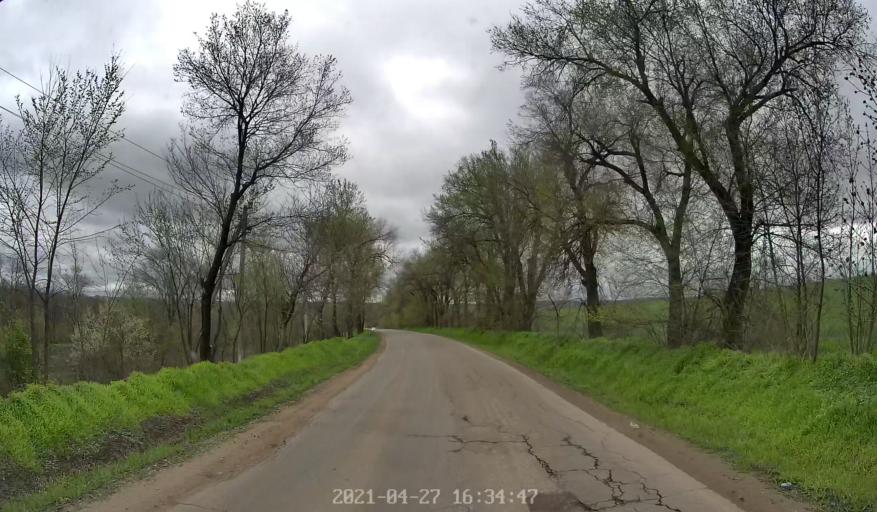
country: MD
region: Chisinau
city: Singera
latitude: 46.9331
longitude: 29.0470
